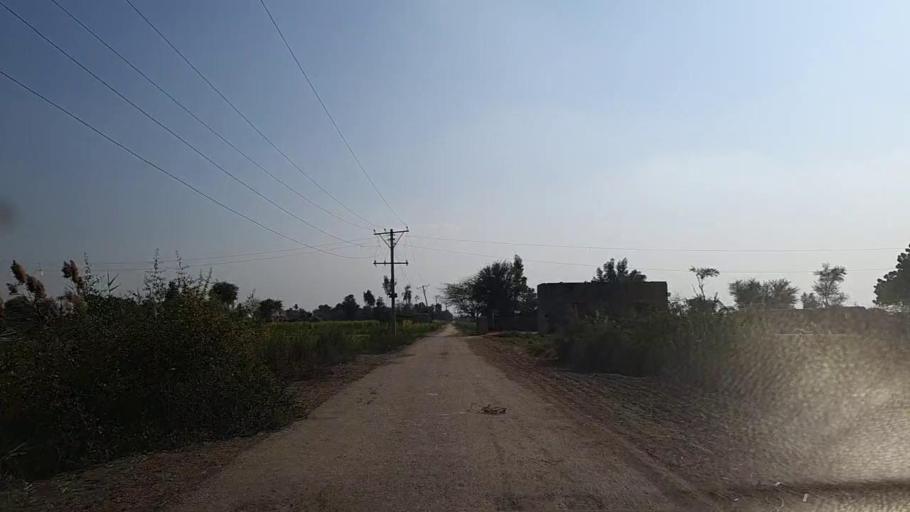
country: PK
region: Sindh
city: Jam Sahib
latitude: 26.2782
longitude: 68.6046
